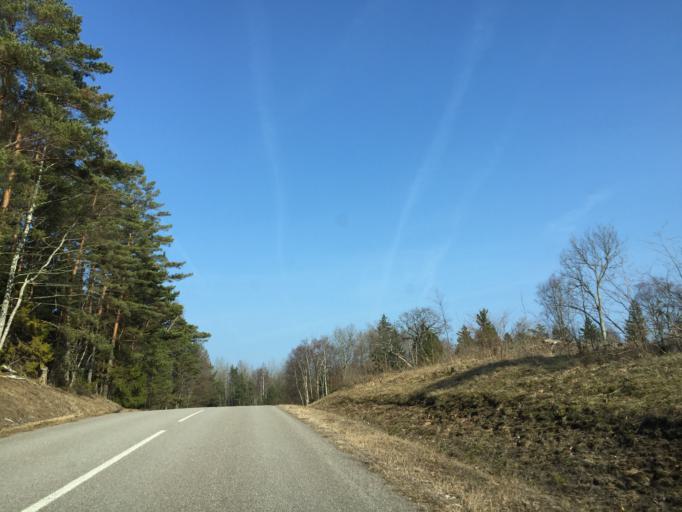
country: EE
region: Saare
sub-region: Kuressaare linn
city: Kuressaare
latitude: 58.0245
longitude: 22.0870
